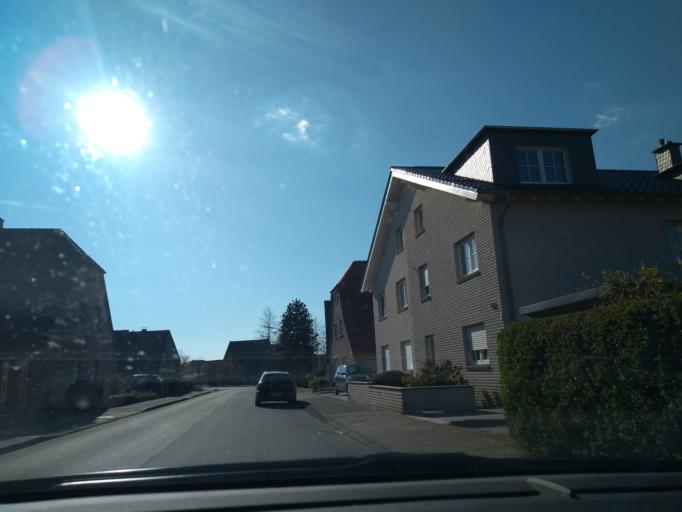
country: DE
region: North Rhine-Westphalia
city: Selm
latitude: 51.6920
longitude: 7.4702
